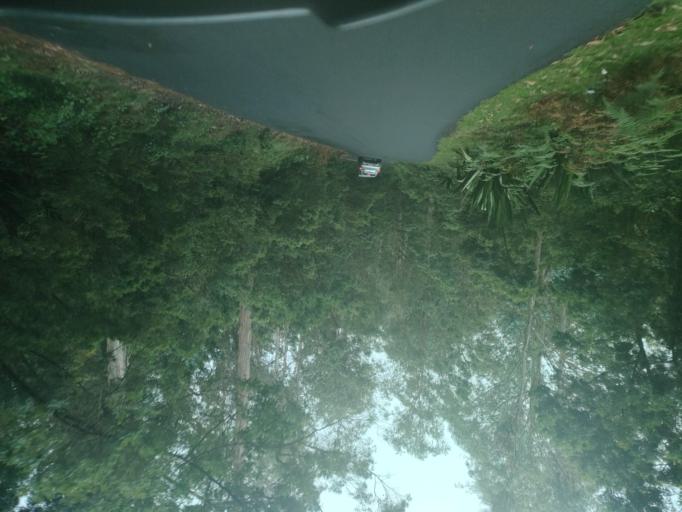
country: IN
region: Tamil Nadu
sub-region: Dindigul
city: Kodaikanal
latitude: 10.2419
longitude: 77.3591
